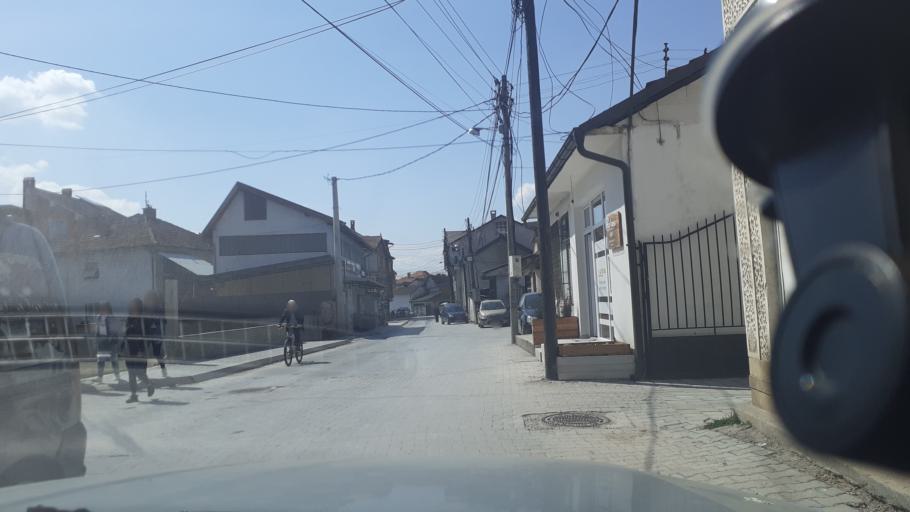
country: MK
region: Tetovo
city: Tetovo
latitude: 42.0045
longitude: 20.9693
